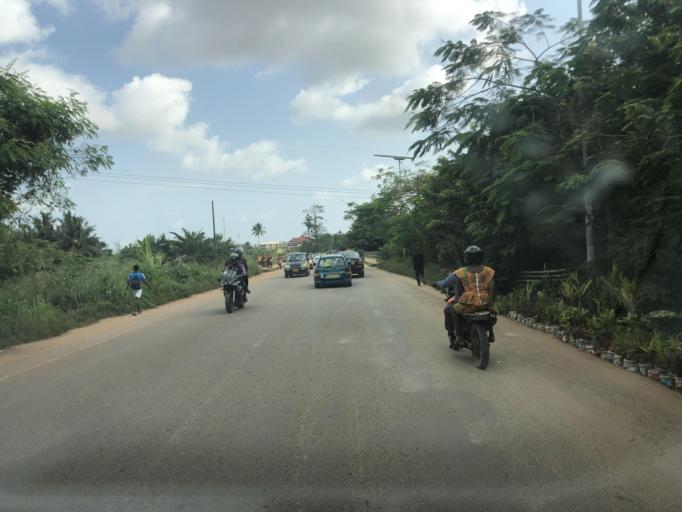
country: GH
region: Central
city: Cape Coast
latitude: 5.1480
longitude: -1.2878
